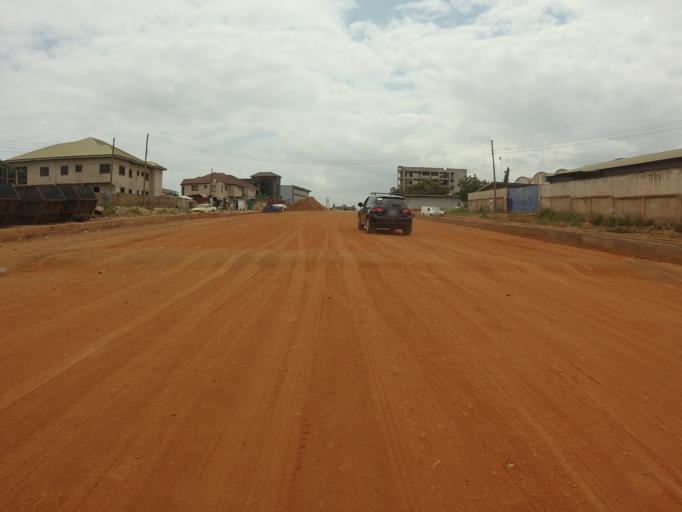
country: GH
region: Greater Accra
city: Medina Estates
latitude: 5.6259
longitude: -0.1502
